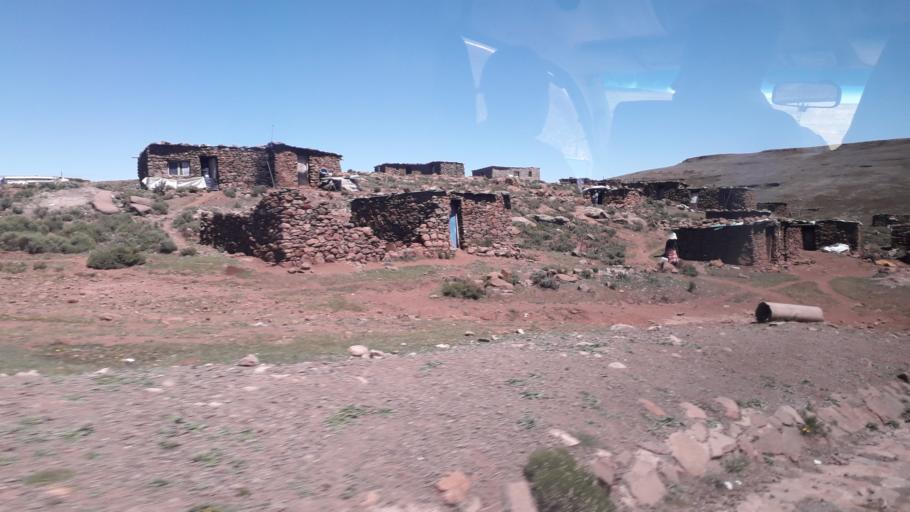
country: LS
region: Mokhotlong
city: Mokhotlong
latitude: -29.0126
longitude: 28.8441
